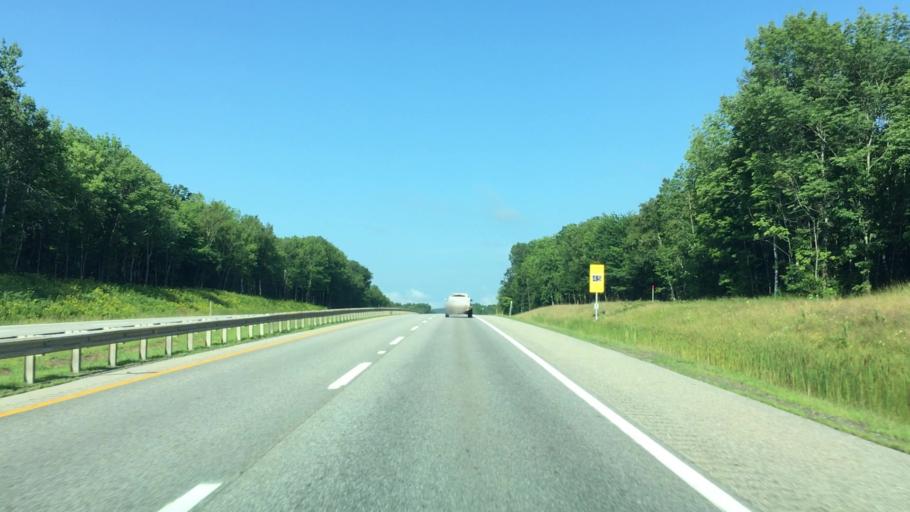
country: US
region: Maine
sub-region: Androscoggin County
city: Sabattus
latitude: 44.1252
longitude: -69.9830
